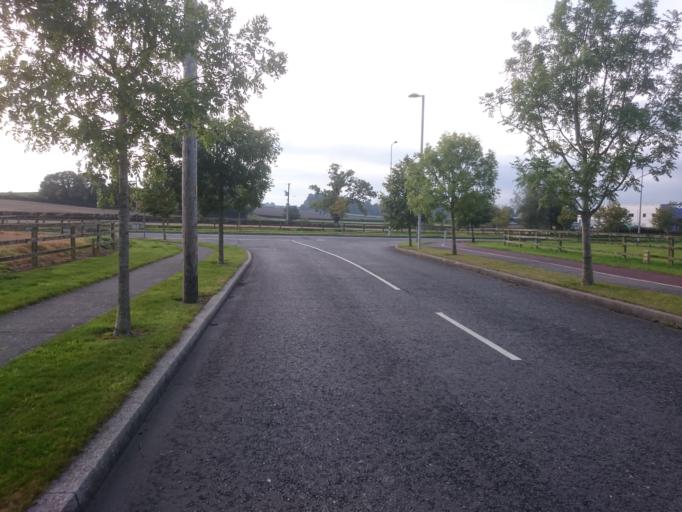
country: IE
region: Leinster
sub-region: Kilkenny
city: Kilkenny
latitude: 52.6320
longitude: -7.2477
